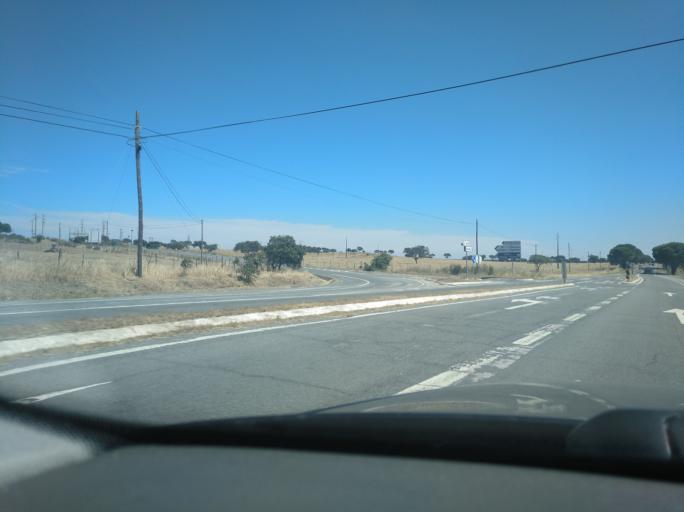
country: PT
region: Beja
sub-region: Almodovar
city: Almodovar
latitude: 37.5784
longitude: -8.0768
